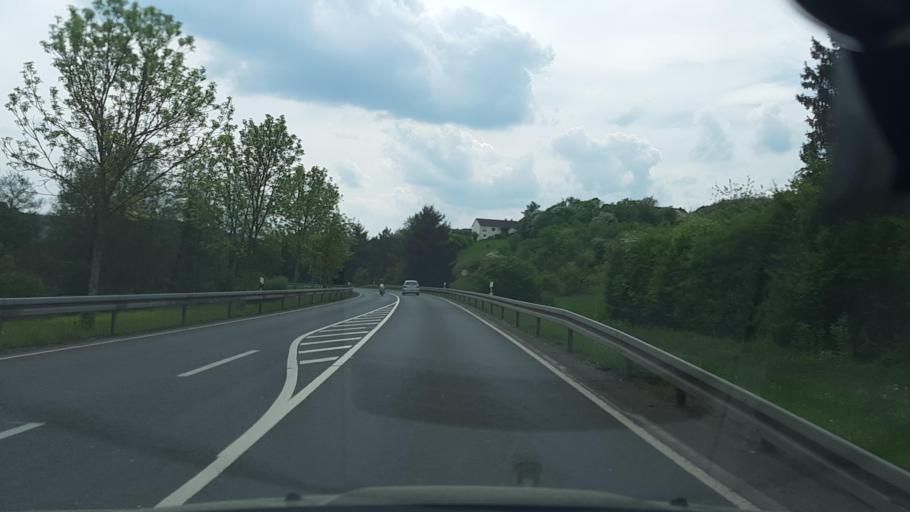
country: DE
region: Hesse
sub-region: Regierungsbezirk Giessen
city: Ehringshausen
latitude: 50.6104
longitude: 8.3840
